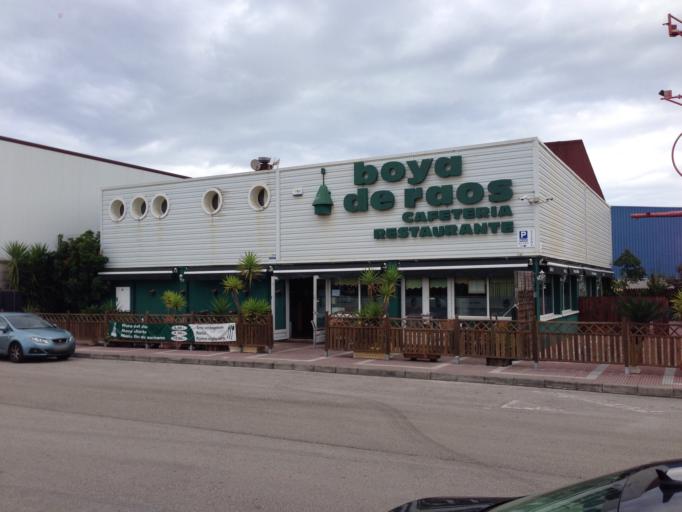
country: ES
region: Cantabria
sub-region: Provincia de Cantabria
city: El Astillero
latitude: 43.4303
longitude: -3.8171
